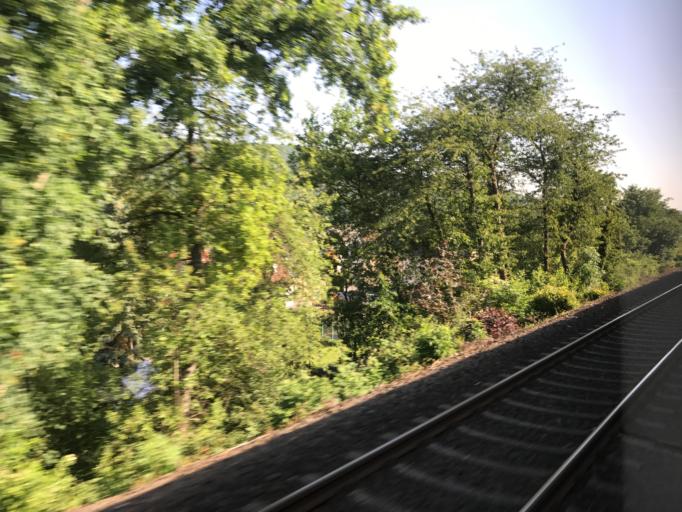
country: DE
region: Rheinland-Pfalz
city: Hintertiefenbach
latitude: 49.7130
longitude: 7.3678
